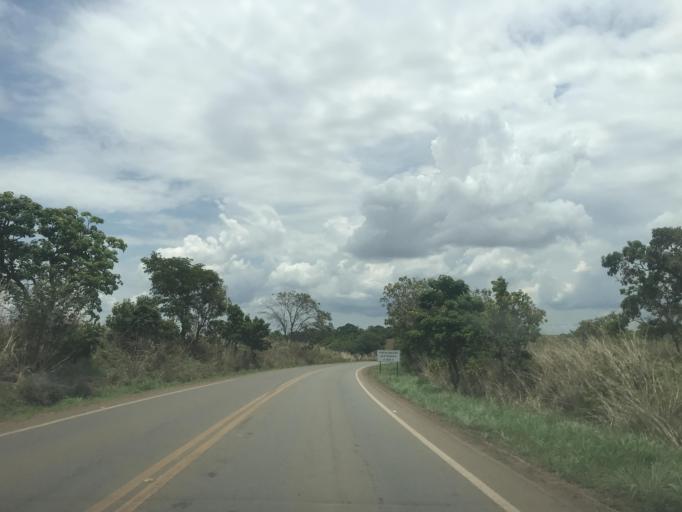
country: BR
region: Goias
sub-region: Vianopolis
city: Vianopolis
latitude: -16.7404
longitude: -48.4482
